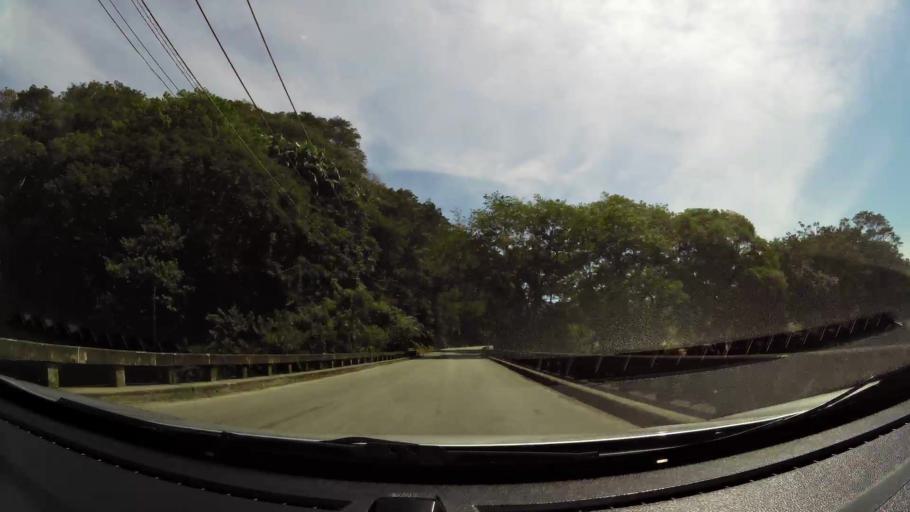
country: CR
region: San Jose
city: San Isidro
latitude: 9.2582
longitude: -83.8635
